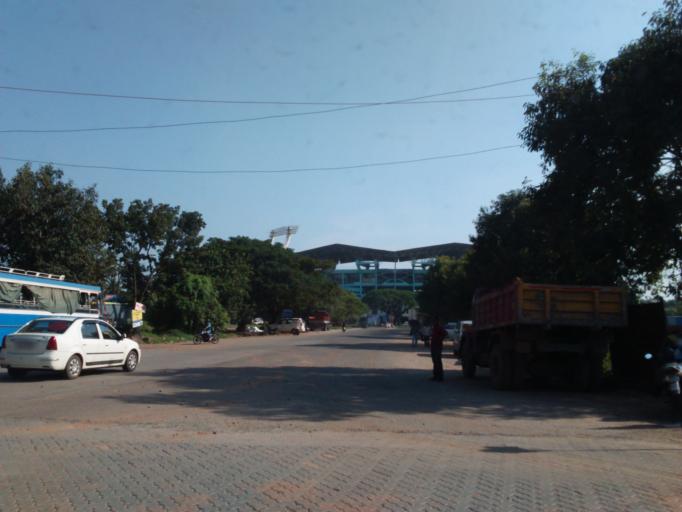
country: IN
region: Kerala
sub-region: Ernakulam
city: Elur
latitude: 10.0005
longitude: 76.2998
